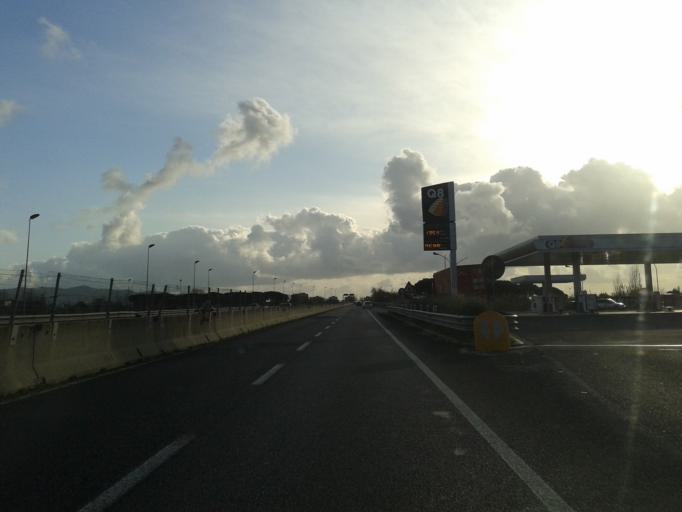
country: IT
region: Tuscany
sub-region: Provincia di Livorno
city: Livorno
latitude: 43.5512
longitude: 10.3428
